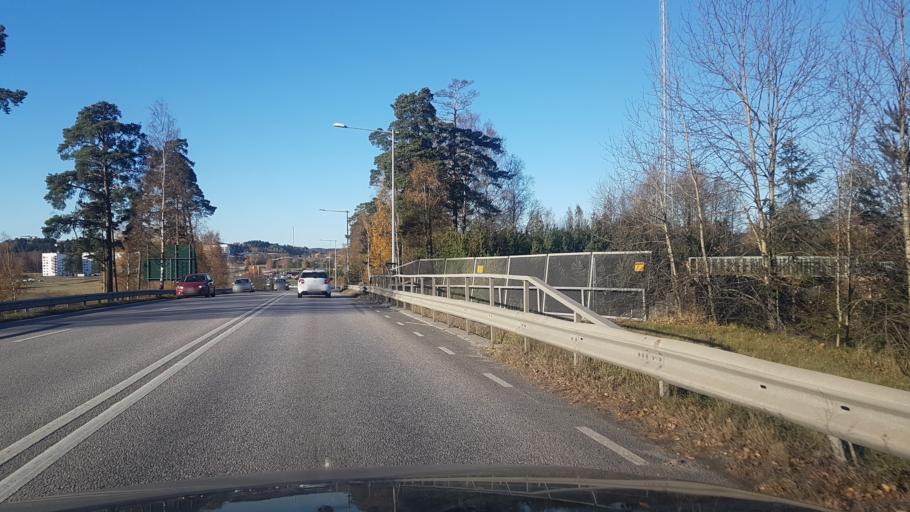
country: SE
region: Stockholm
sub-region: Sigtuna Kommun
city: Marsta
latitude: 59.6142
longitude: 17.8615
